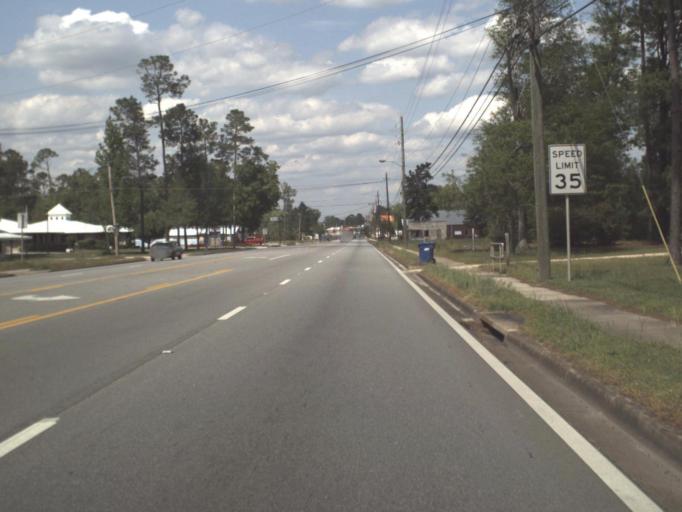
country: US
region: Florida
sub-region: Escambia County
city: Century
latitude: 30.9747
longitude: -87.2629
